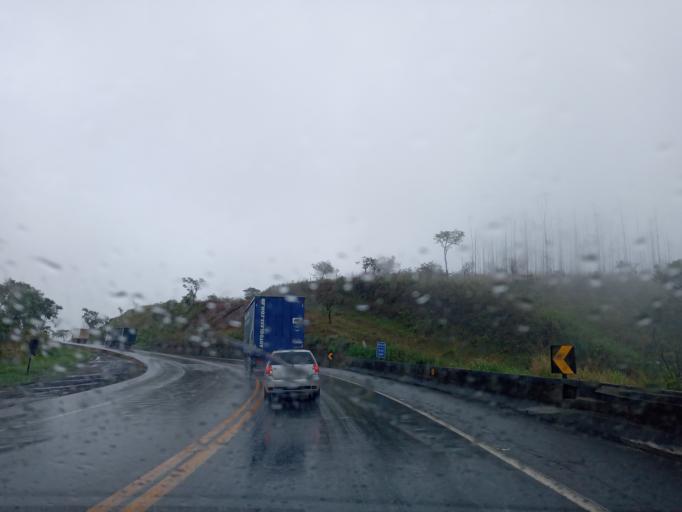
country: BR
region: Minas Gerais
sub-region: Luz
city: Luz
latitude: -19.7162
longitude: -45.8829
